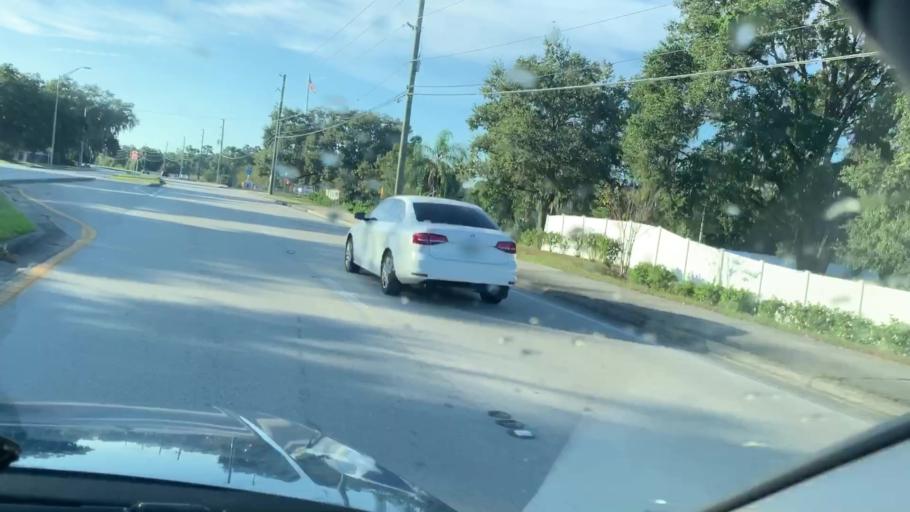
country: US
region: Florida
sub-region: Polk County
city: Gibsonia
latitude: 28.0905
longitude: -81.9965
